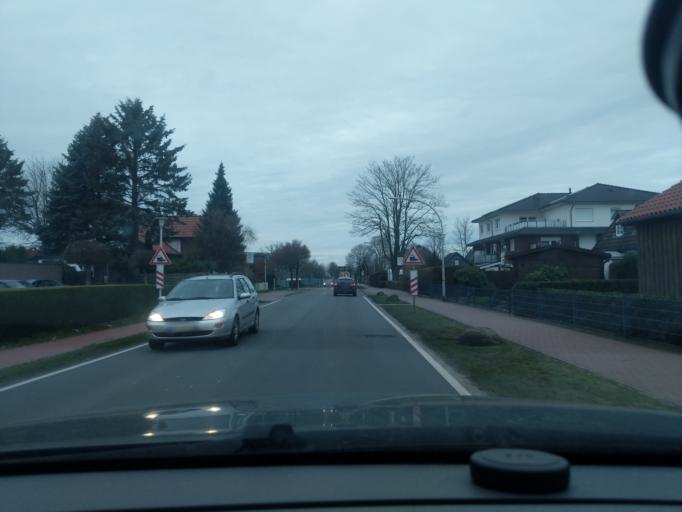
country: DE
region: Lower Saxony
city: Apensen
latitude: 53.4387
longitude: 9.6115
